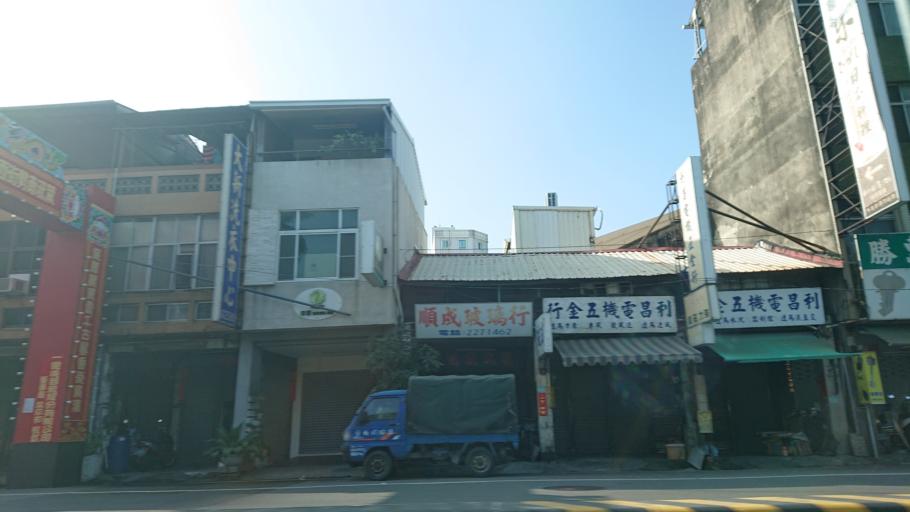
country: TW
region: Taiwan
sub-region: Tainan
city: Tainan
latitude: 22.9965
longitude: 120.1931
